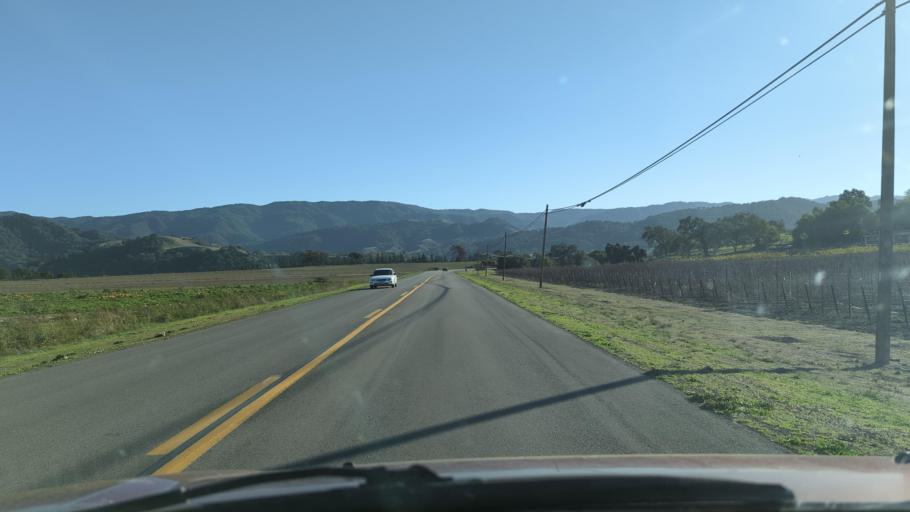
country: US
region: California
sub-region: Santa Barbara County
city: Santa Ynez
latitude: 34.5958
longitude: -120.0982
